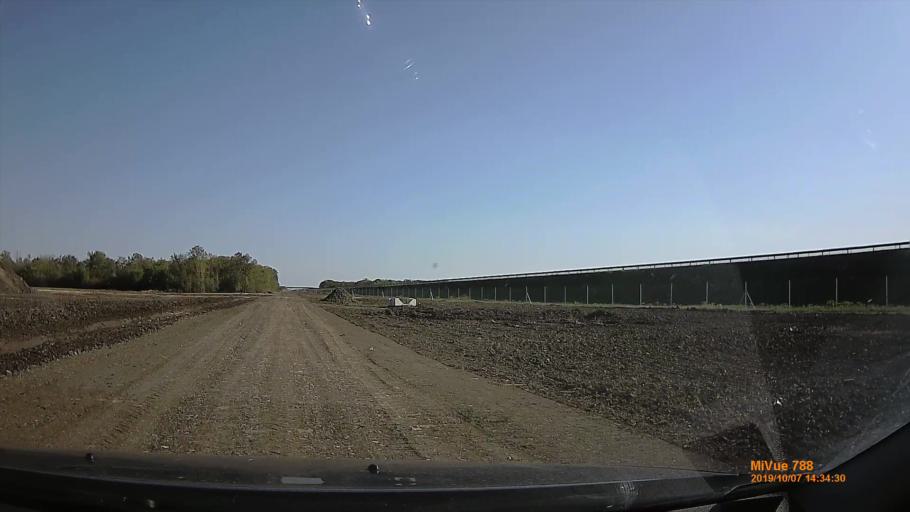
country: HU
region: Jasz-Nagykun-Szolnok
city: Kunszentmarton
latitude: 46.8606
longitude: 20.3033
